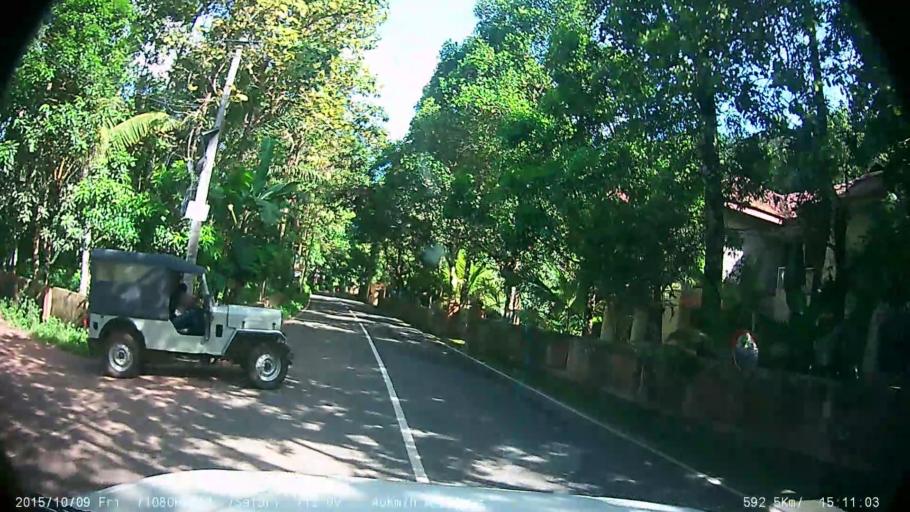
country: IN
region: Kerala
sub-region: Ernakulam
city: Piravam
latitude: 9.8768
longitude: 76.5769
